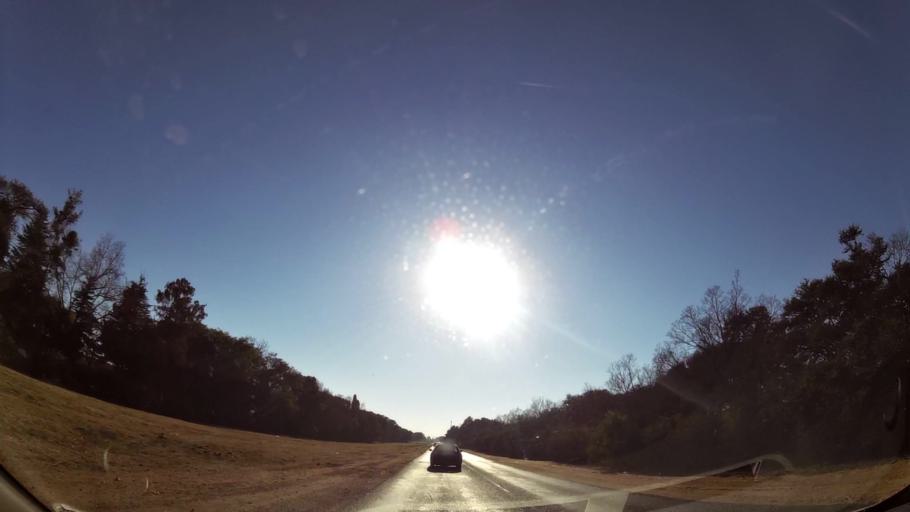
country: ZA
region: Gauteng
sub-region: Ekurhuleni Metropolitan Municipality
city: Tembisa
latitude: -26.0539
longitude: 28.2343
